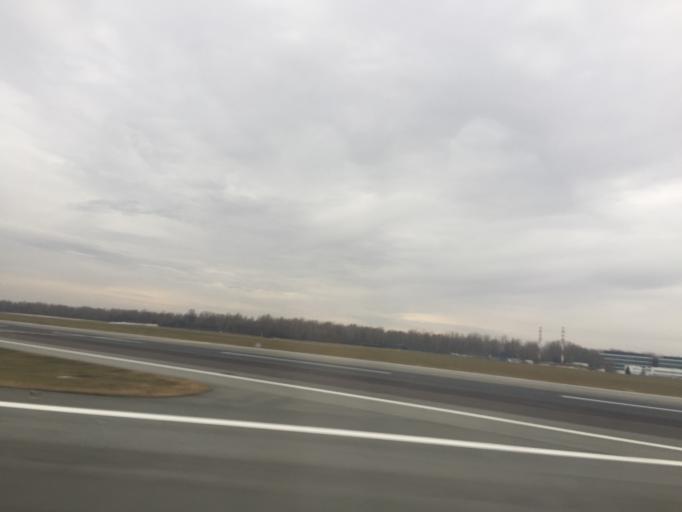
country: PL
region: Masovian Voivodeship
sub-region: Warszawa
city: Wlochy
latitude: 52.1654
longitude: 20.9685
